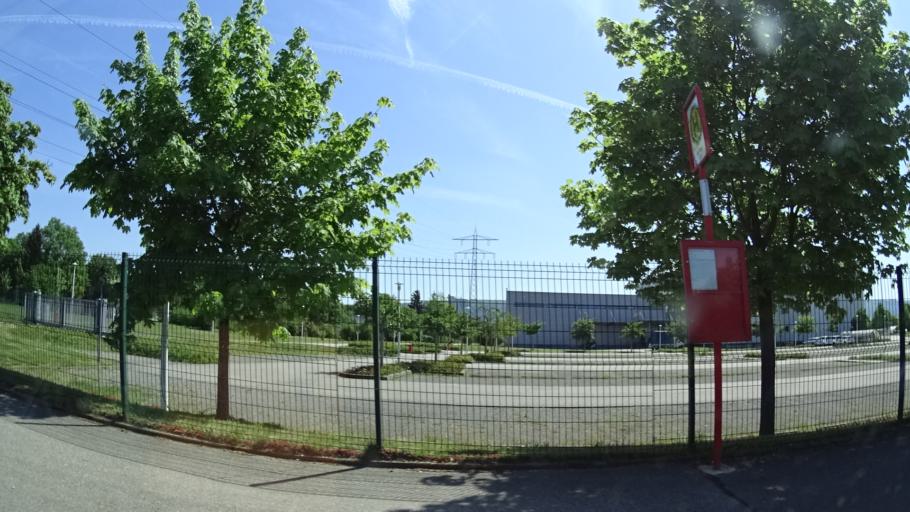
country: DE
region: Baden-Wuerttemberg
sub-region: Karlsruhe Region
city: Ettlingen
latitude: 48.9430
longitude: 8.3672
